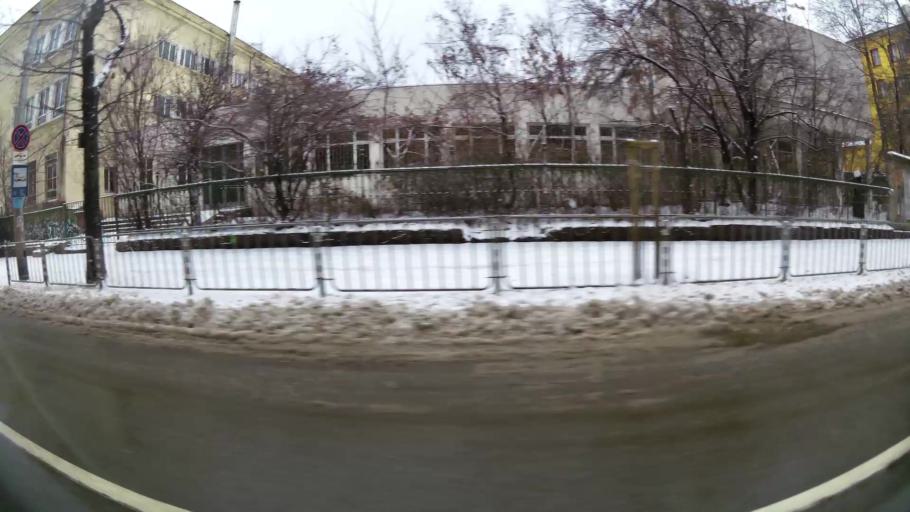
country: BG
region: Sofia-Capital
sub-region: Stolichna Obshtina
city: Sofia
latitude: 42.7000
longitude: 23.2996
